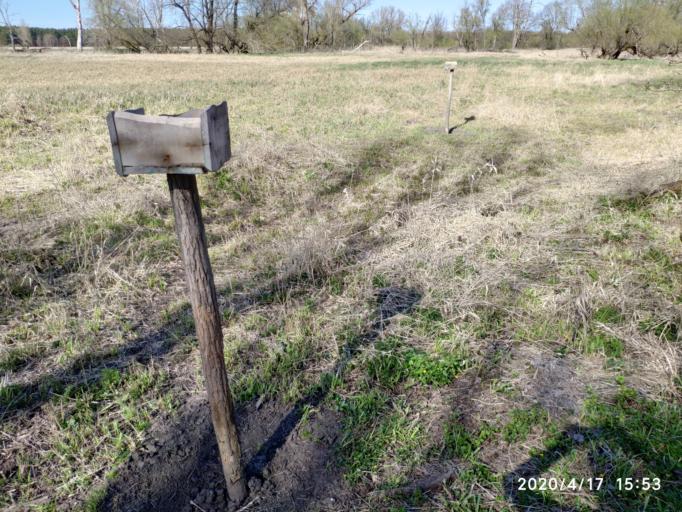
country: PL
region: Lubusz
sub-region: Powiat zielonogorski
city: Czerwiensk
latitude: 52.0385
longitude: 15.5047
